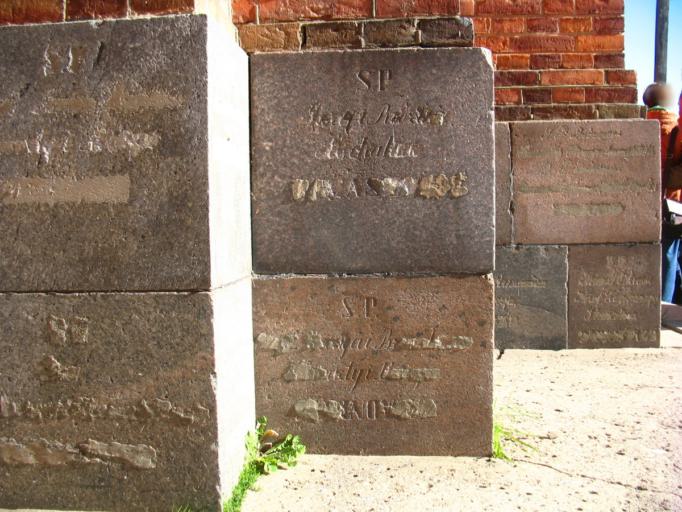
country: BY
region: Grodnenskaya
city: Shchuchin
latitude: 53.7616
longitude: 24.8266
